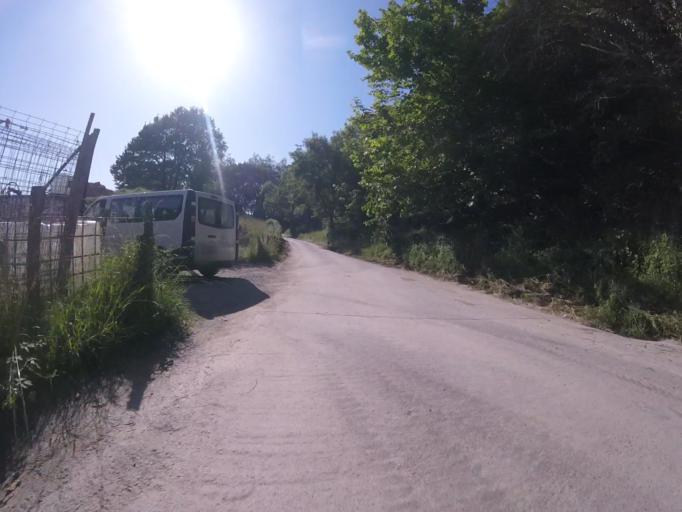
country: ES
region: Basque Country
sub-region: Provincia de Guipuzcoa
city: Astigarraga
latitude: 43.2941
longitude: -1.9306
